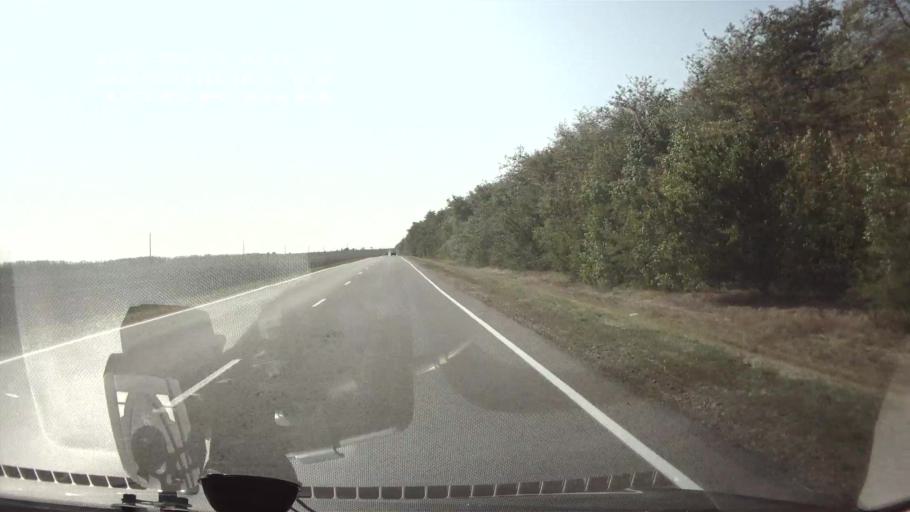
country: RU
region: Krasnodarskiy
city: Novopokrovskaya
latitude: 45.8945
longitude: 40.7210
